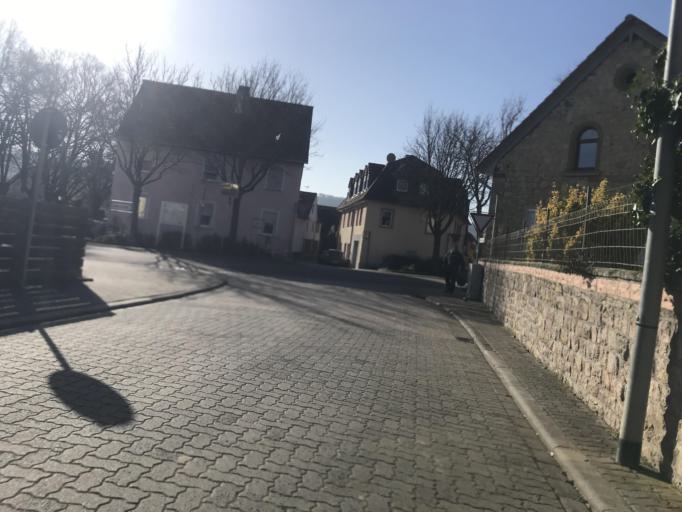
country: DE
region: Rheinland-Pfalz
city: Sankt Johann
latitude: 49.8689
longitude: 8.0178
